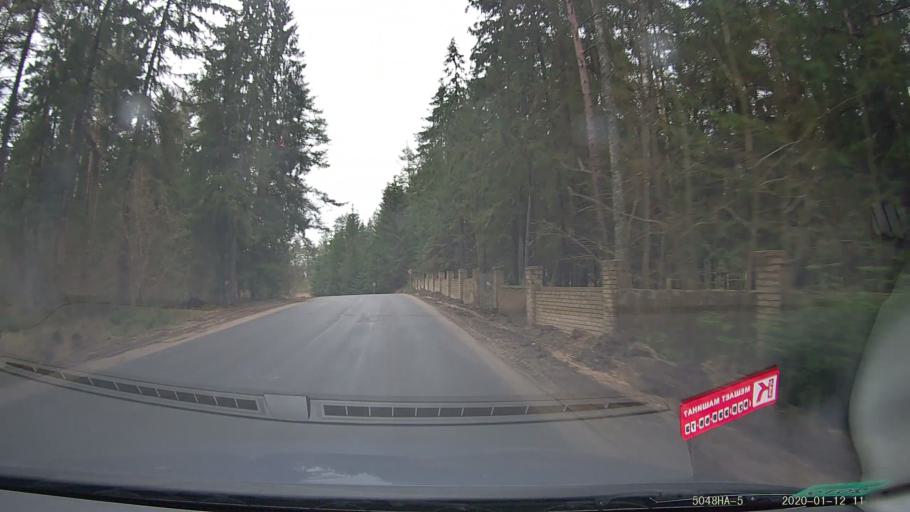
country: BY
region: Minsk
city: Rakaw
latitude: 53.9586
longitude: 27.1183
